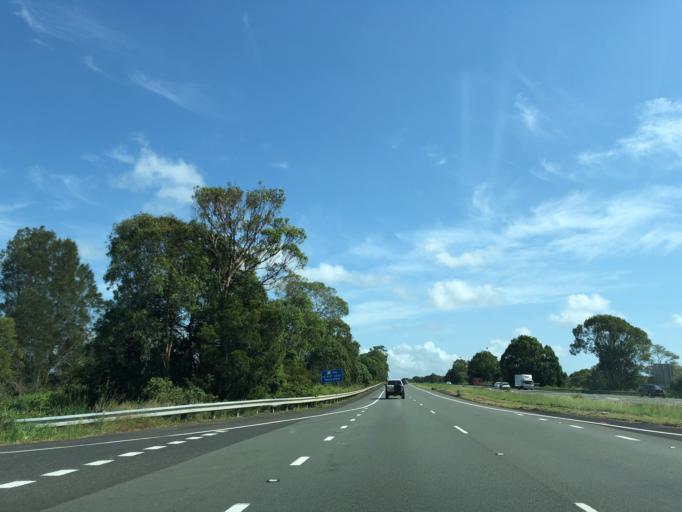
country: AU
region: New South Wales
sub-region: Byron Shire
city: Brunswick Heads
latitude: -28.6084
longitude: 153.5463
